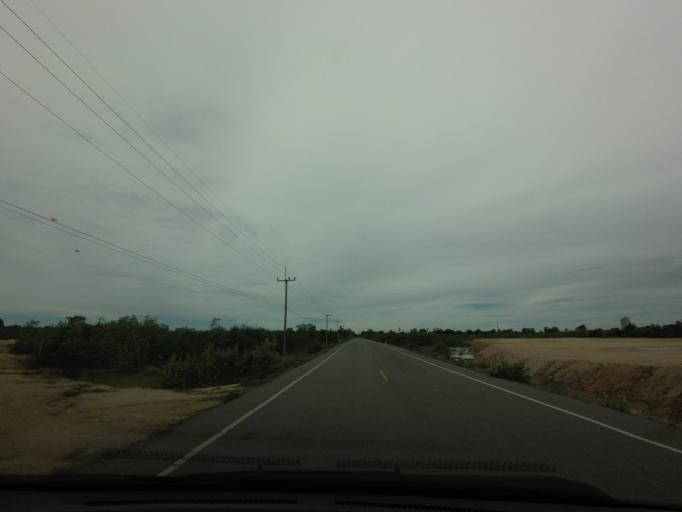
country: TH
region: Phetchaburi
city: Cha-am
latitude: 12.8426
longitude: 99.9824
